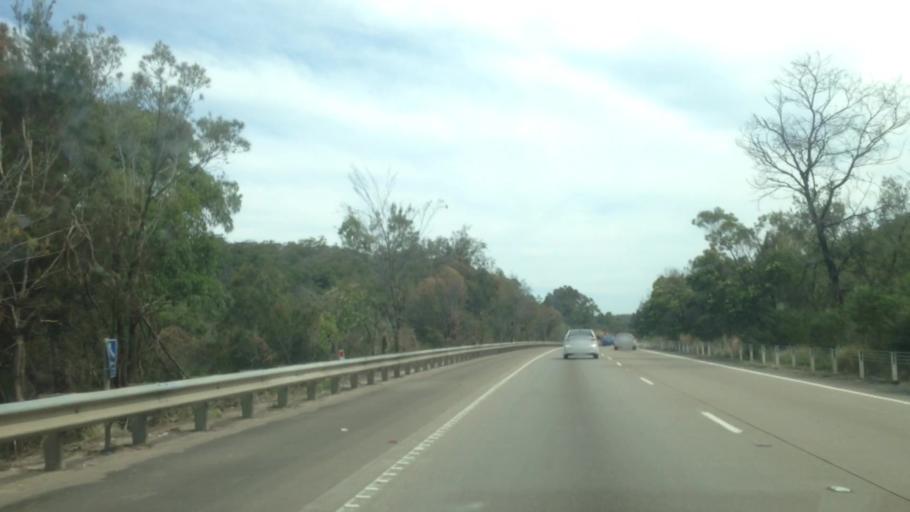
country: AU
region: New South Wales
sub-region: Lake Macquarie Shire
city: Fennell Bay
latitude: -32.9772
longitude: 151.5298
